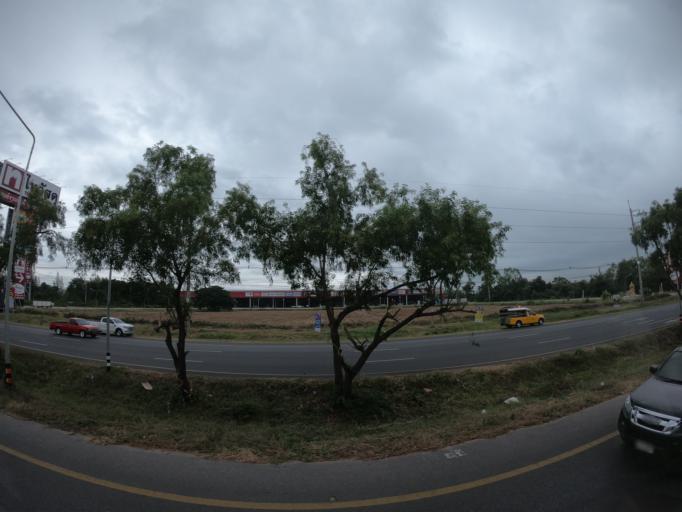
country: TH
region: Roi Et
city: Roi Et
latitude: 16.0557
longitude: 103.6199
